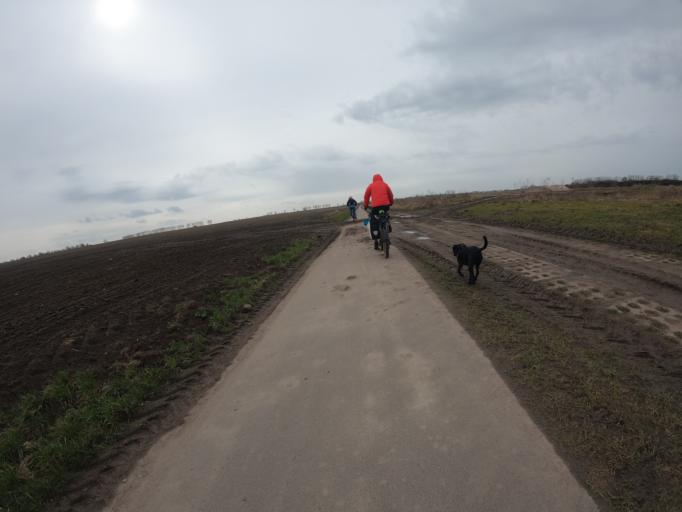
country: PL
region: West Pomeranian Voivodeship
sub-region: Powiat gryficki
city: Mrzezyno
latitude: 54.1060
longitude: 15.2904
